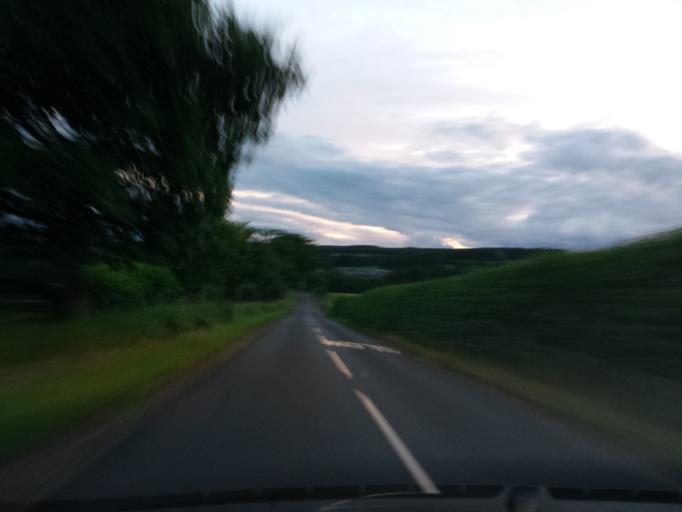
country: GB
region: Scotland
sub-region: The Scottish Borders
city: Duns
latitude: 55.8349
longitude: -2.2884
